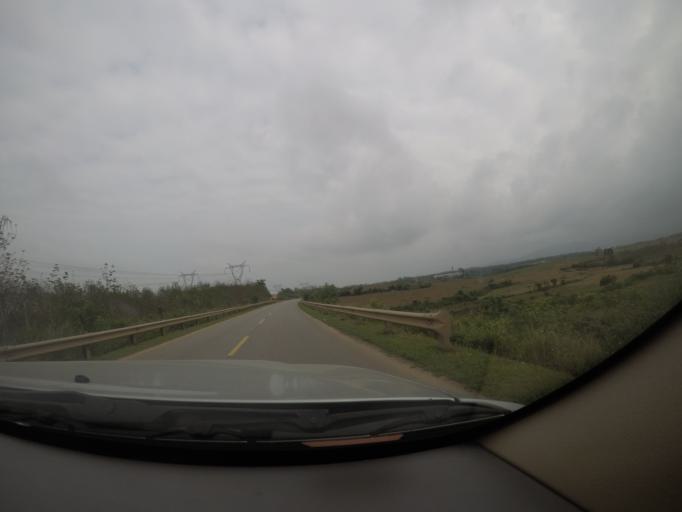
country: VN
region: Quang Binh
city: Hoan Lao
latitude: 17.5062
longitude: 106.5031
